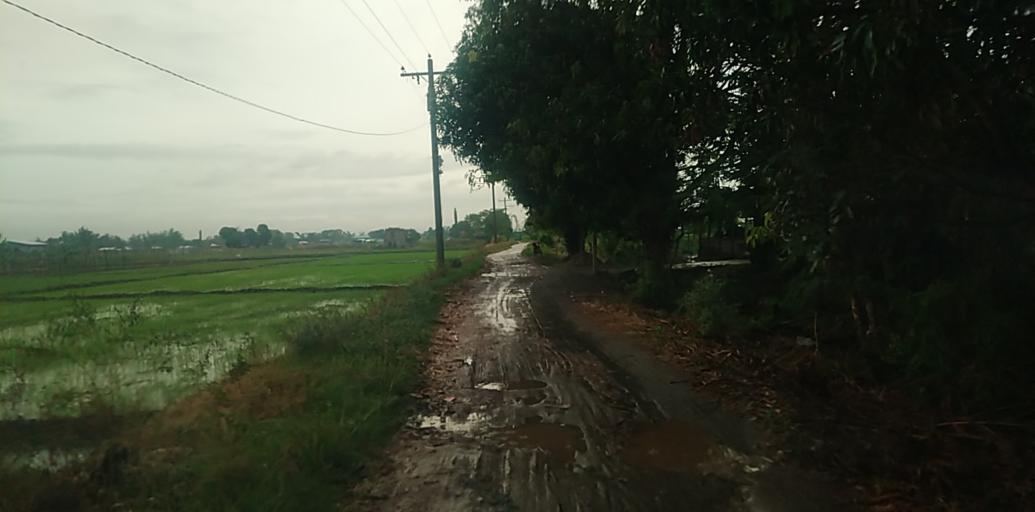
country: PH
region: Central Luzon
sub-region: Province of Pampanga
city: Panlinlang
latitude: 15.1597
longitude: 120.7162
